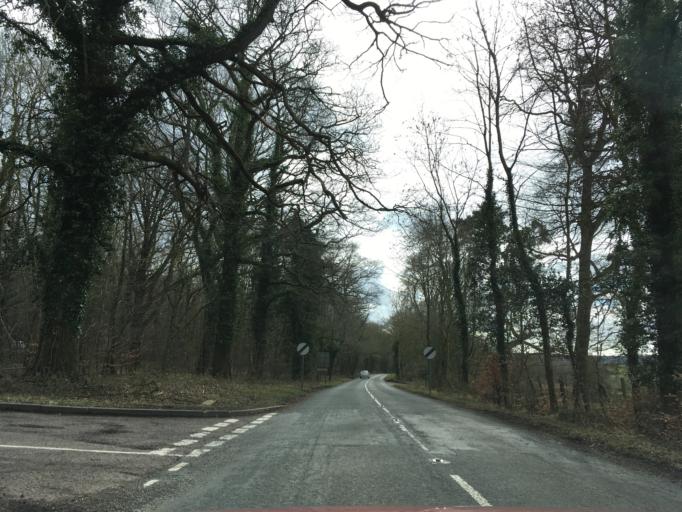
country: GB
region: England
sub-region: Gloucestershire
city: Coleford
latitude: 51.7763
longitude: -2.6096
